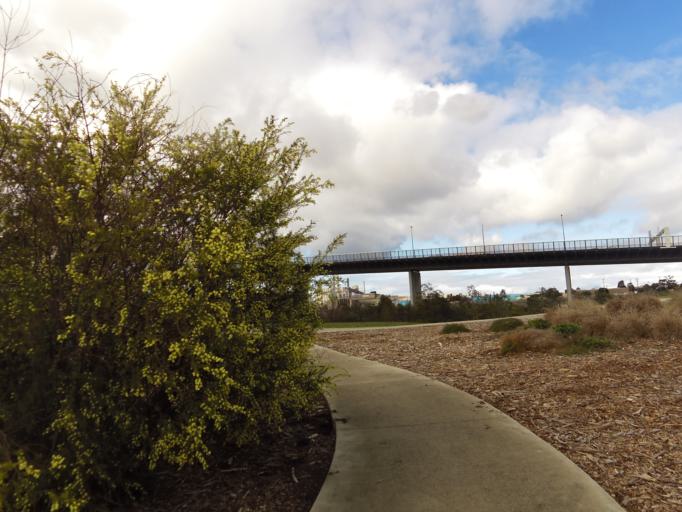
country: AU
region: Victoria
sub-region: Hobsons Bay
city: Spotswood
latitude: -37.8239
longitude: 144.8910
